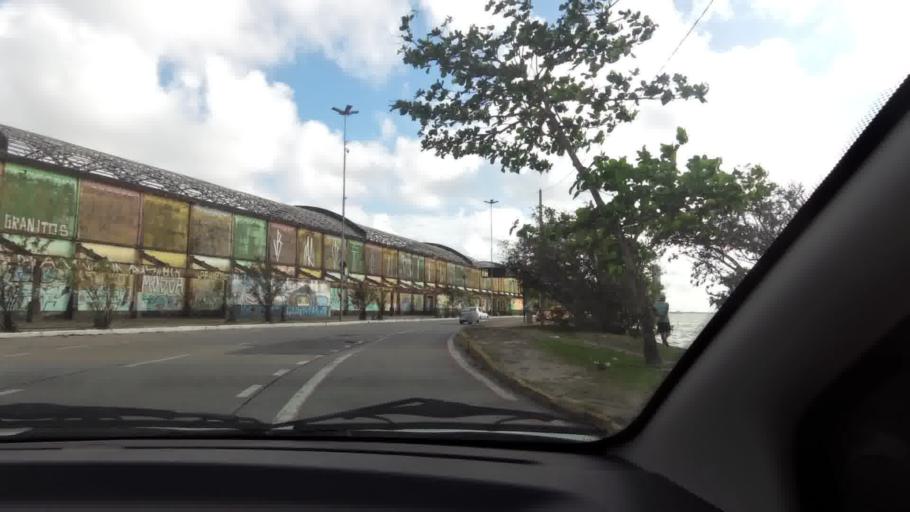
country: BR
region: Pernambuco
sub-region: Recife
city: Recife
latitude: -8.0771
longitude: -34.8906
